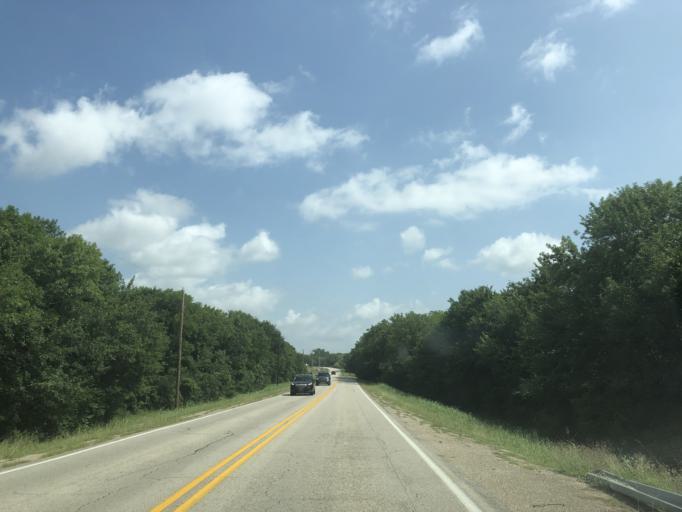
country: US
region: Texas
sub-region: Dallas County
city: Sunnyvale
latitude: 32.8206
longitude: -96.5595
